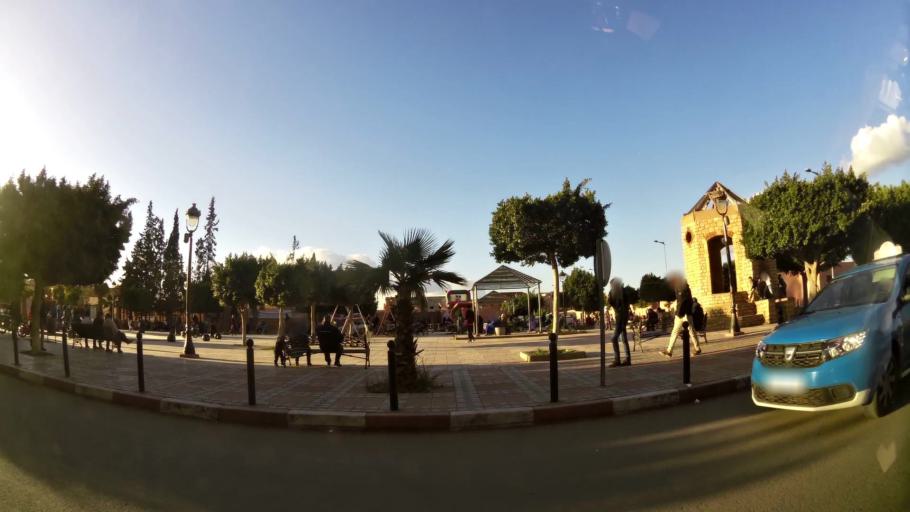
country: MA
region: Marrakech-Tensift-Al Haouz
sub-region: Kelaa-Des-Sraghna
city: Sidi Abdallah
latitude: 32.2395
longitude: -7.9556
